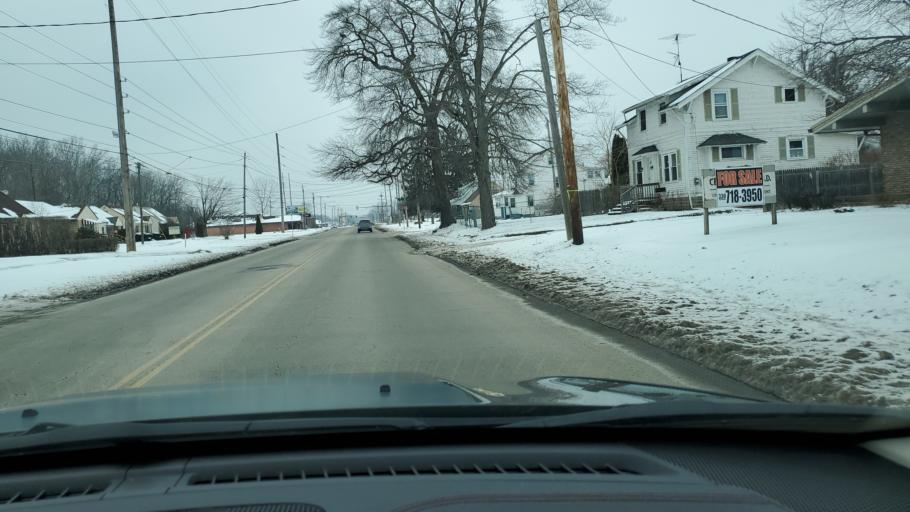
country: US
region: Ohio
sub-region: Trumbull County
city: Leavittsburg
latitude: 41.2480
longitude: -80.8485
